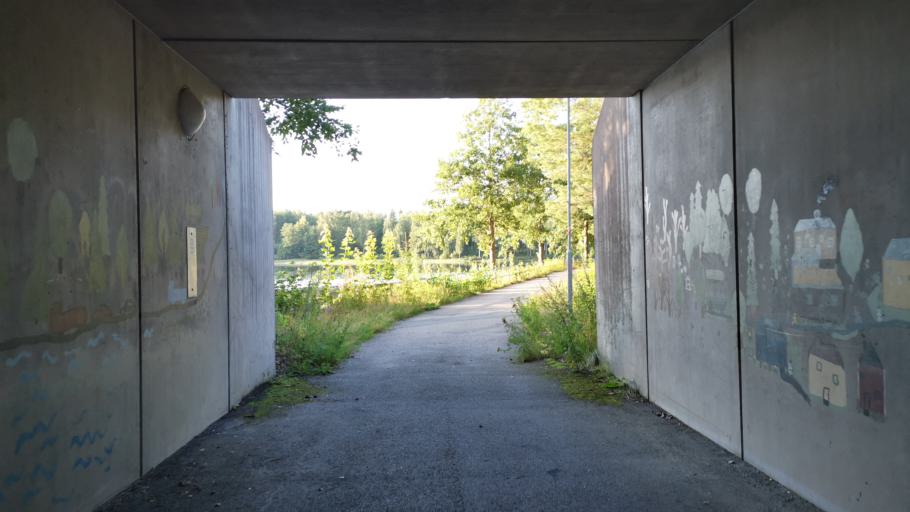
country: SE
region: OEstergoetland
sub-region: Norrkopings Kommun
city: Krokek
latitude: 58.7260
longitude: 16.4290
